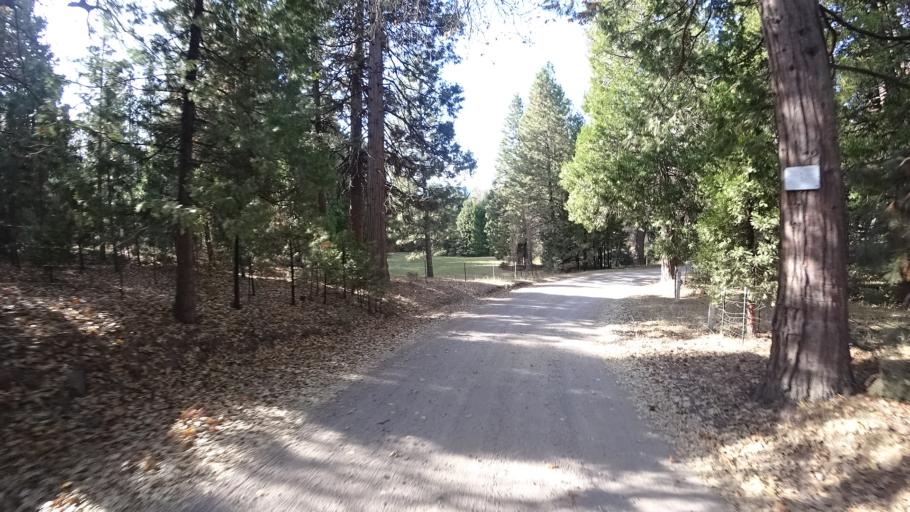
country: US
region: California
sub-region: Siskiyou County
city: Weed
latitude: 41.4341
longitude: -122.4168
